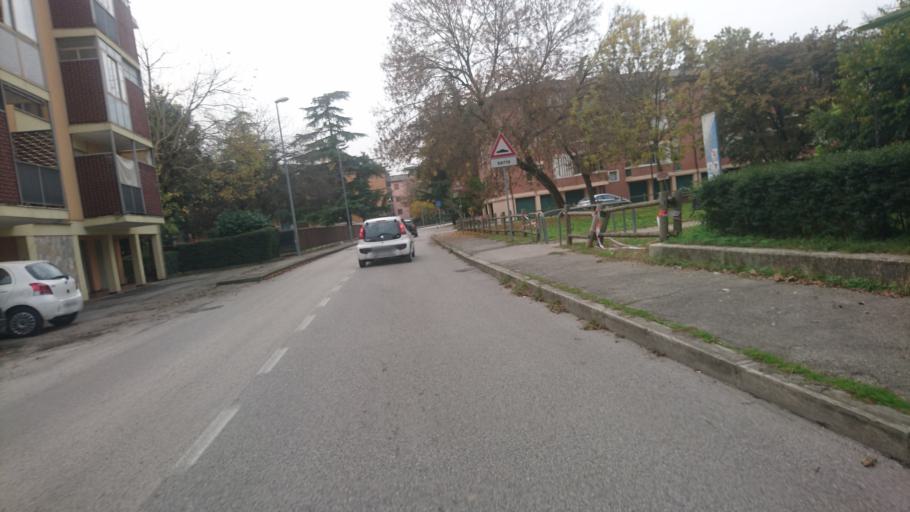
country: IT
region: Veneto
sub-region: Provincia di Padova
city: Padova
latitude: 45.4245
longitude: 11.9072
